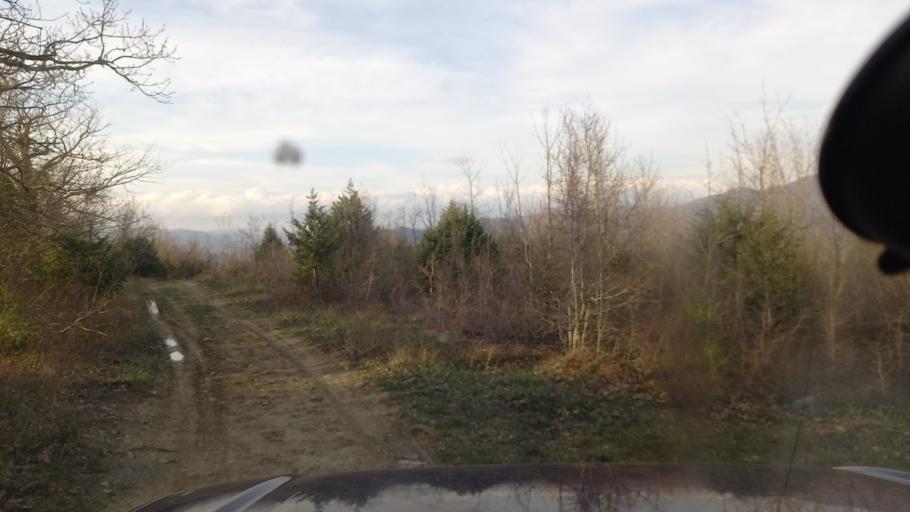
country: RU
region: Krasnodarskiy
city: Arkhipo-Osipovka
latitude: 44.3595
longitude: 38.5534
